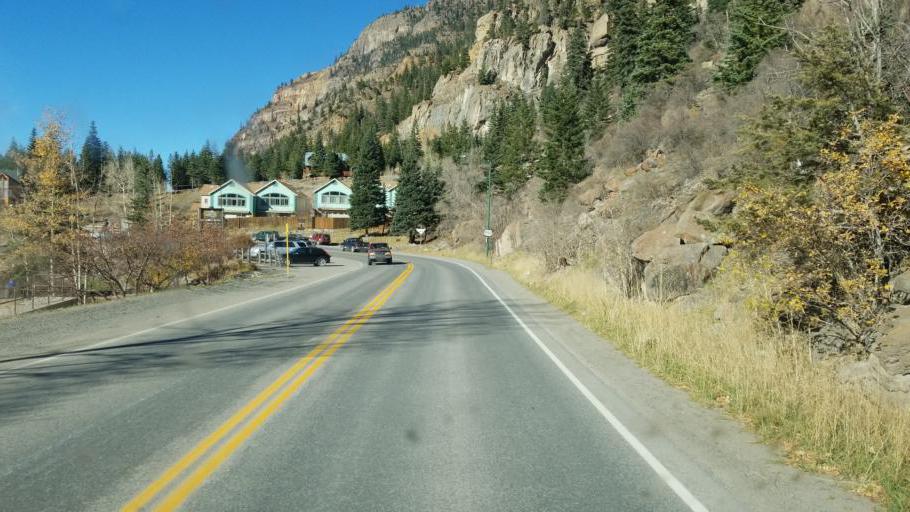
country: US
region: Colorado
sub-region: Ouray County
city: Ouray
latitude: 38.0285
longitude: -107.6715
